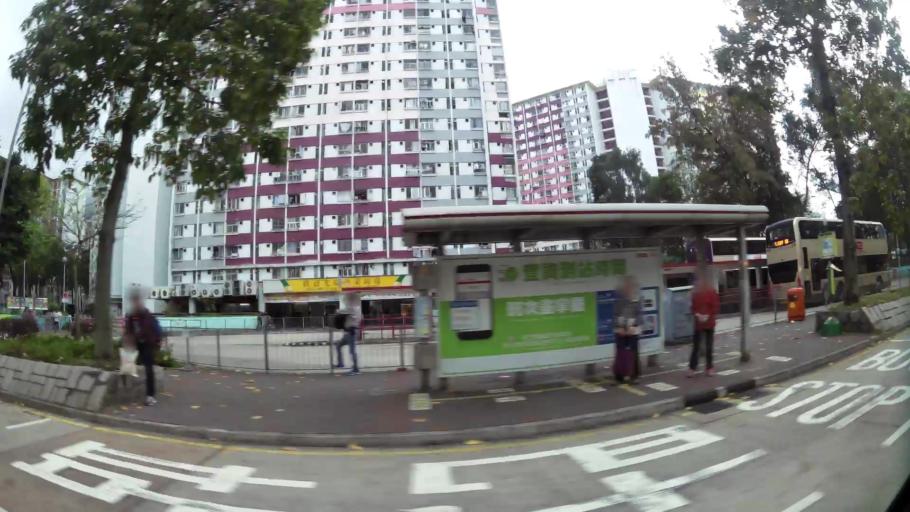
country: HK
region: Kowloon City
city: Kowloon
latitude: 22.3286
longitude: 114.2084
